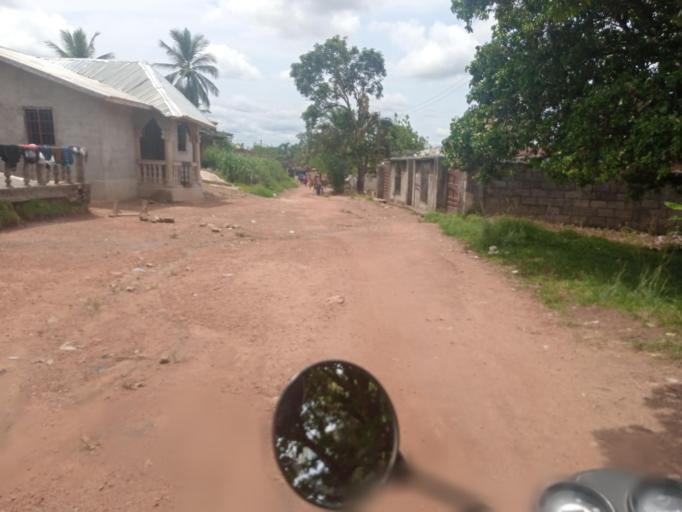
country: SL
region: Southern Province
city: Bo
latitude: 7.9536
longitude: -11.7180
